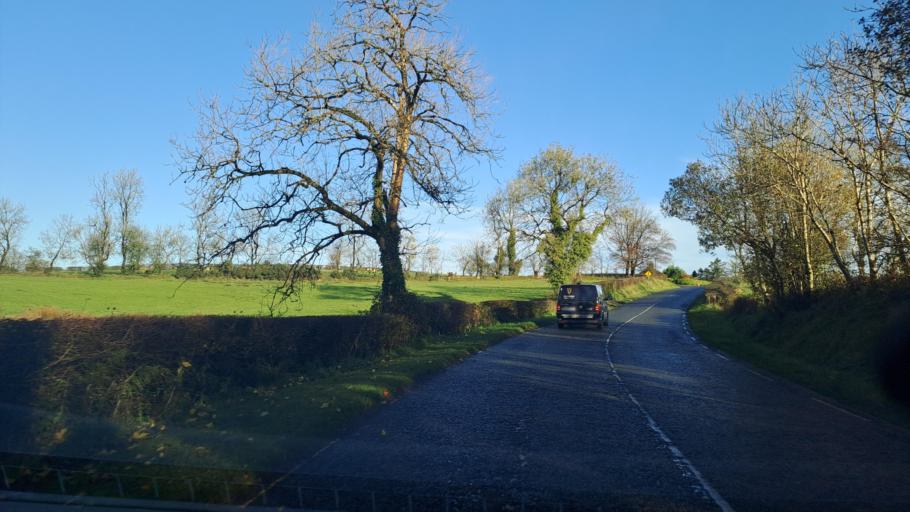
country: IE
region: Ulster
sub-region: County Monaghan
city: Monaghan
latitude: 54.1798
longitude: -6.9960
